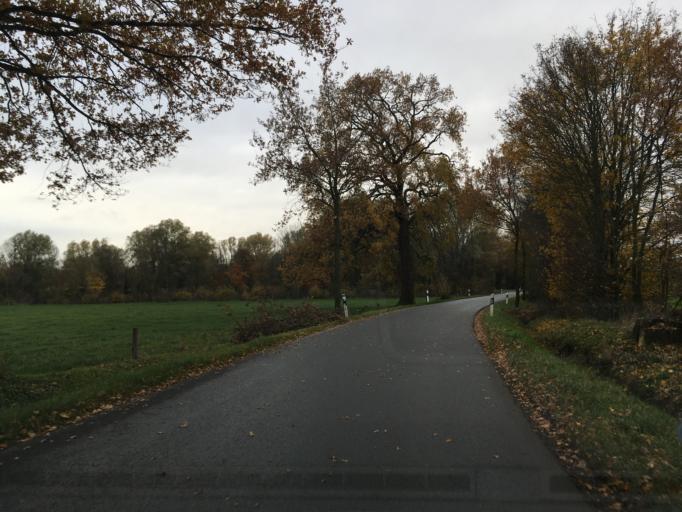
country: DE
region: North Rhine-Westphalia
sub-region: Regierungsbezirk Munster
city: Gescher
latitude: 51.9738
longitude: 7.0100
